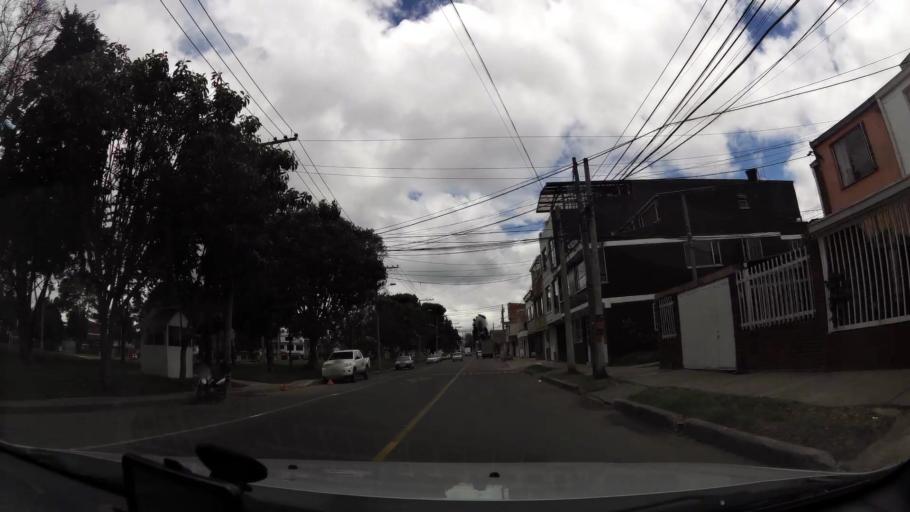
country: CO
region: Bogota D.C.
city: Bogota
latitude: 4.6082
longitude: -74.1189
